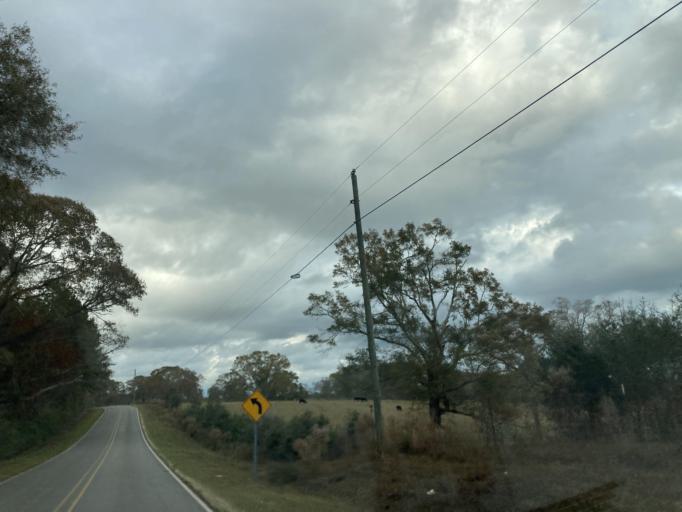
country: US
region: Mississippi
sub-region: Marion County
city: Columbia
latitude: 31.1856
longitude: -89.6642
